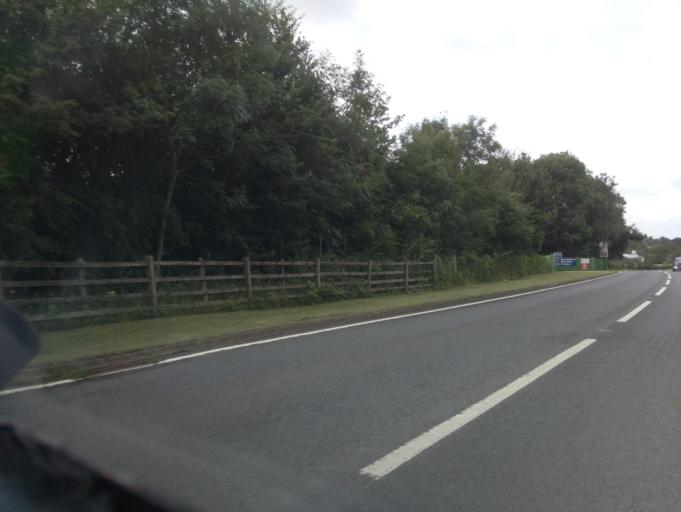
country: GB
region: England
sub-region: Warwickshire
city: Long Itchington
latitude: 52.2815
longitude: -1.3603
